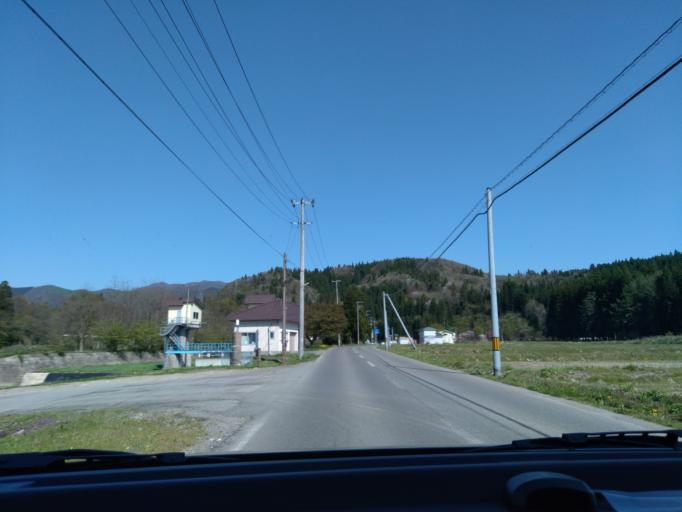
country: JP
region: Akita
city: Yokotemachi
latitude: 39.4158
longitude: 140.5861
